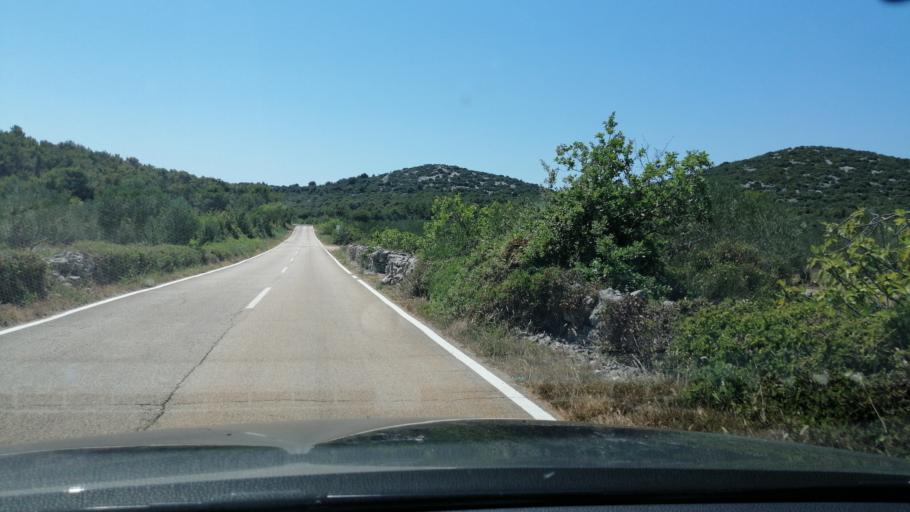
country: HR
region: Sibensko-Kniniska
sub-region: Grad Sibenik
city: Pirovac
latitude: 43.8480
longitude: 15.6870
